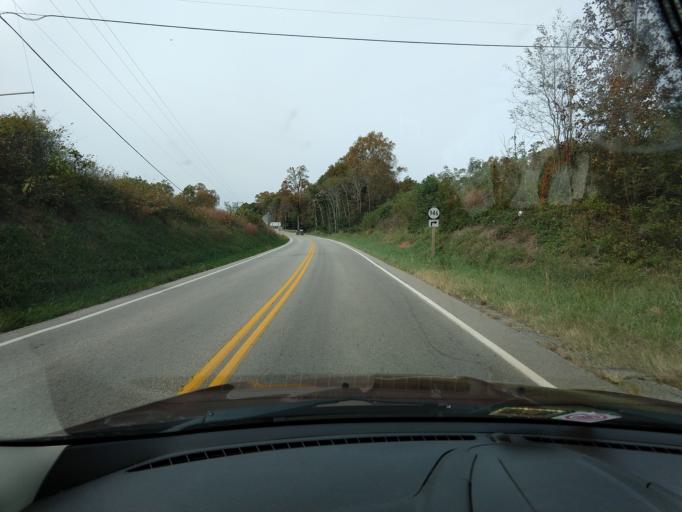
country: US
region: Virginia
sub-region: Franklin County
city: Union Hall
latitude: 36.9836
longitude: -79.6300
